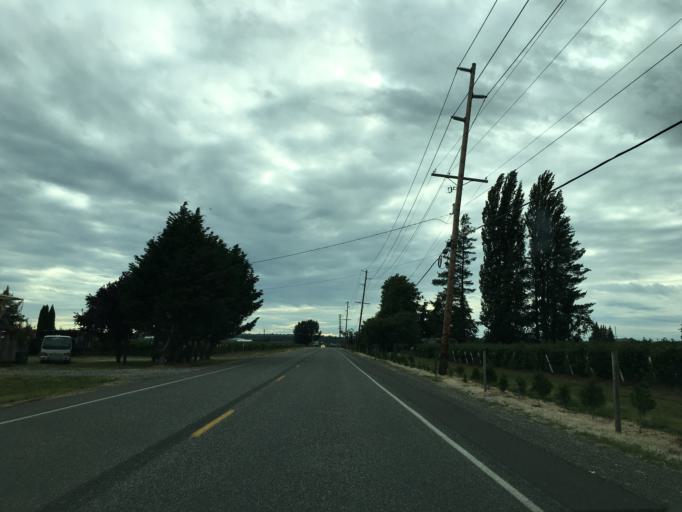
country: US
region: Washington
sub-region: Whatcom County
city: Ferndale
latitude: 48.8880
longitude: -122.5347
